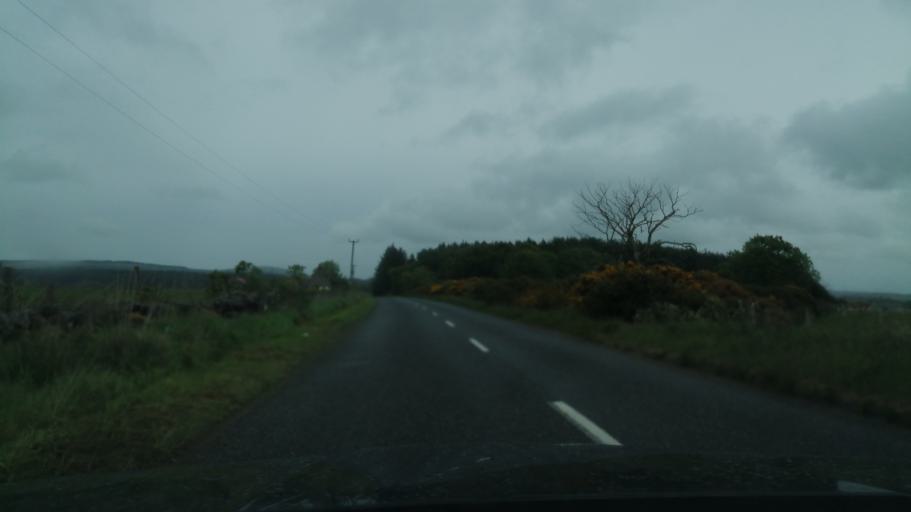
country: GB
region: Scotland
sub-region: Aberdeenshire
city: Portsoy
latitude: 57.6097
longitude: -2.7247
